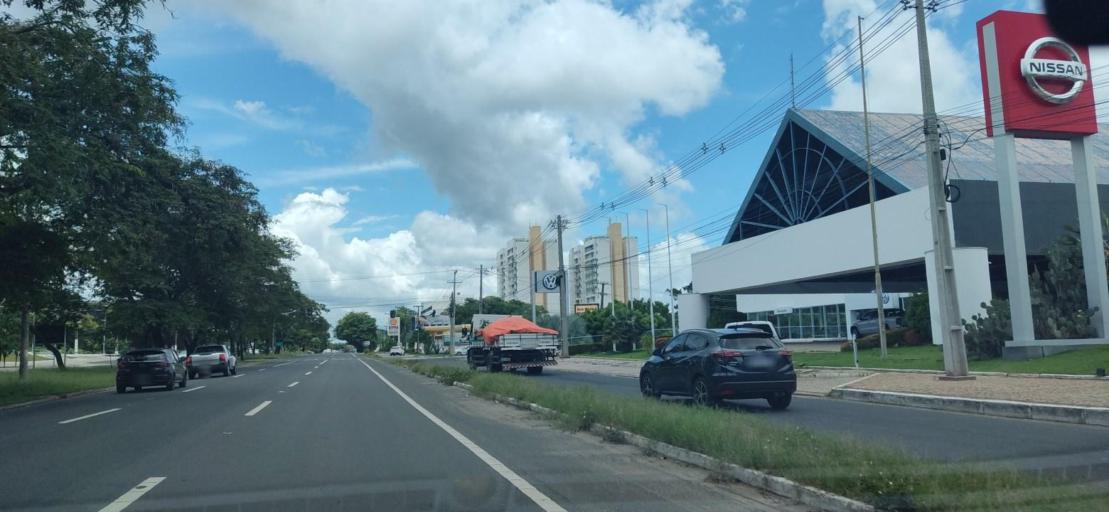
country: BR
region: Piaui
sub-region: Teresina
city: Teresina
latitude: -5.0816
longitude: -42.7669
